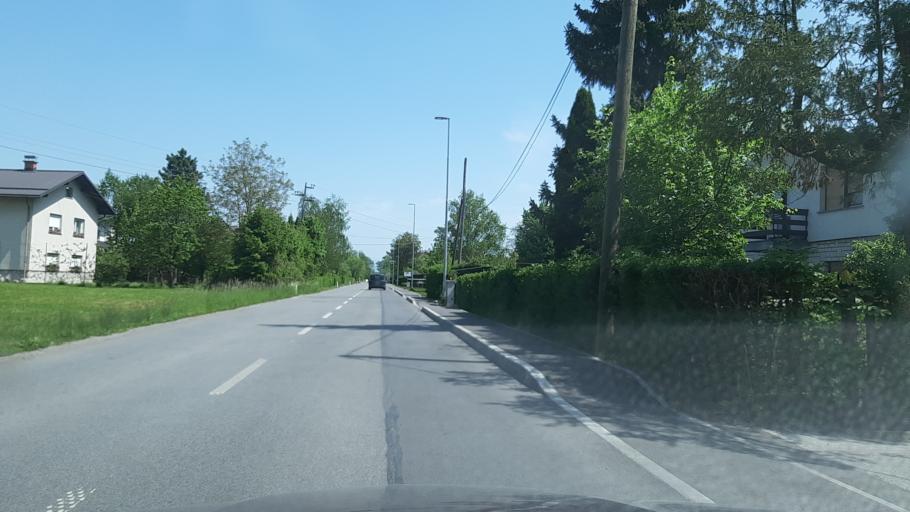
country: SI
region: Brezovica
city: Notranje Gorice
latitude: 45.9745
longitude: 14.4208
